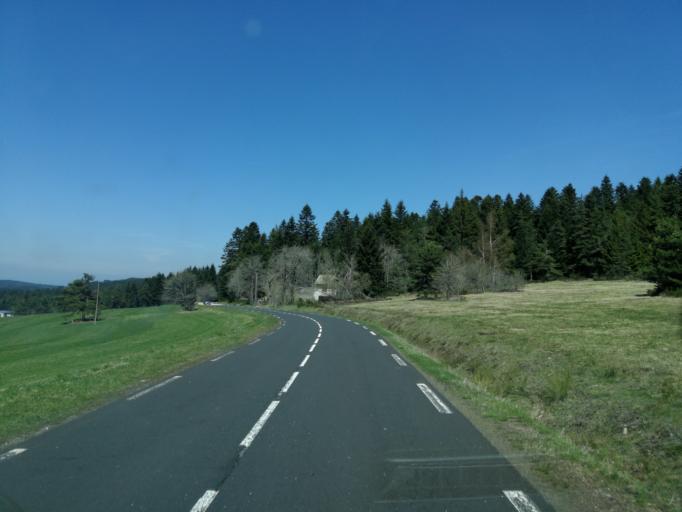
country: FR
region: Rhone-Alpes
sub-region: Departement de l'Ardeche
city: Saint-Agreve
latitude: 45.1021
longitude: 4.4018
